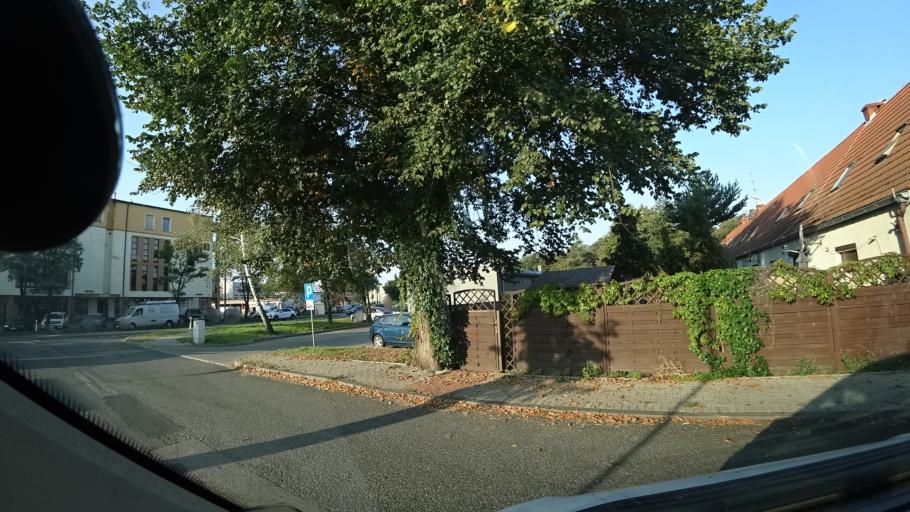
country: PL
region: Opole Voivodeship
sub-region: Powiat kedzierzynsko-kozielski
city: Kedzierzyn-Kozle
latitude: 50.3523
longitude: 18.2349
